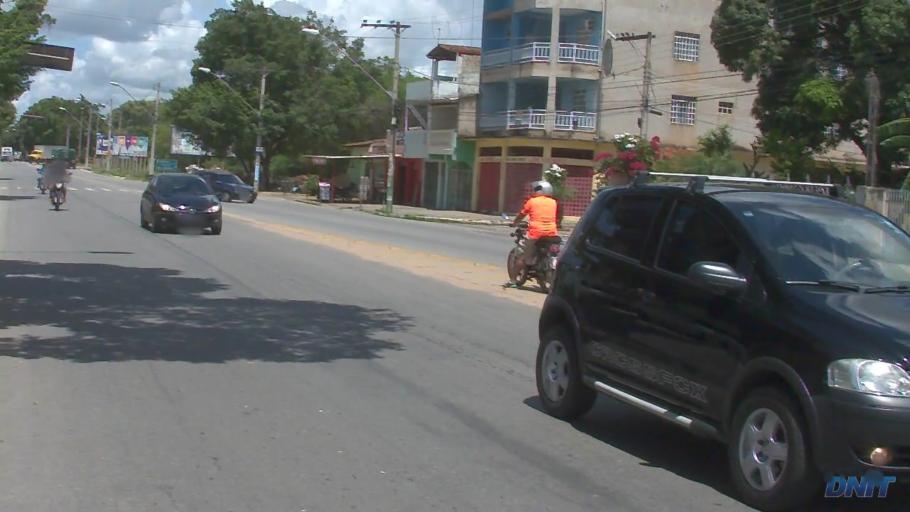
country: BR
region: Minas Gerais
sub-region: Governador Valadares
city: Governador Valadares
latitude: -18.8838
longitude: -41.9671
